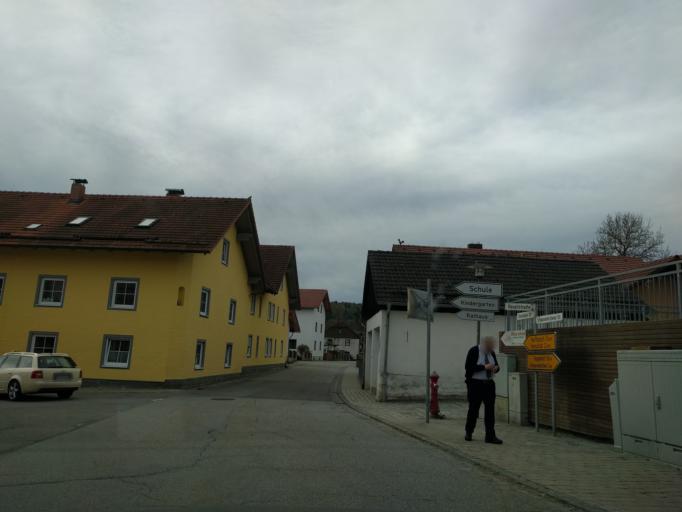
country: DE
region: Bavaria
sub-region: Lower Bavaria
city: Iggensbach
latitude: 48.7289
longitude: 13.1398
